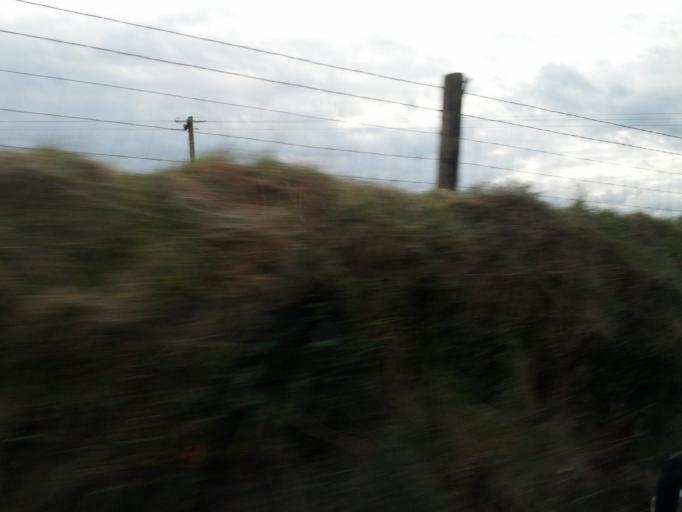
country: IE
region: Connaught
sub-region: County Galway
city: Athenry
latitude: 53.3831
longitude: -8.7207
